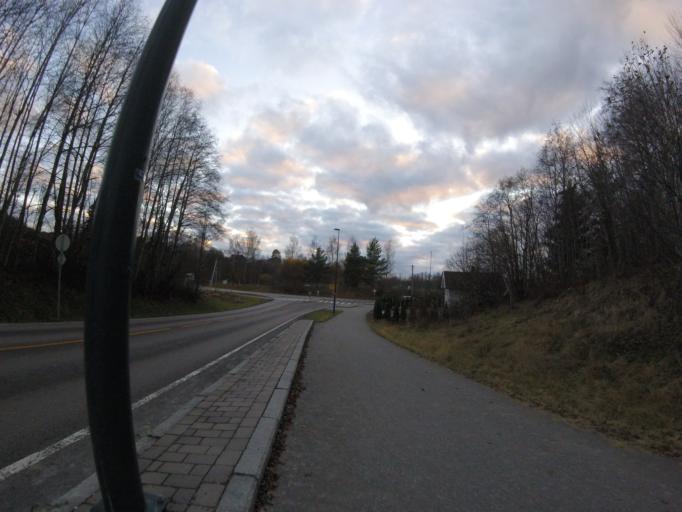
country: NO
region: Akershus
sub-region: Skedsmo
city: Leirsund
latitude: 59.9986
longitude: 11.0985
